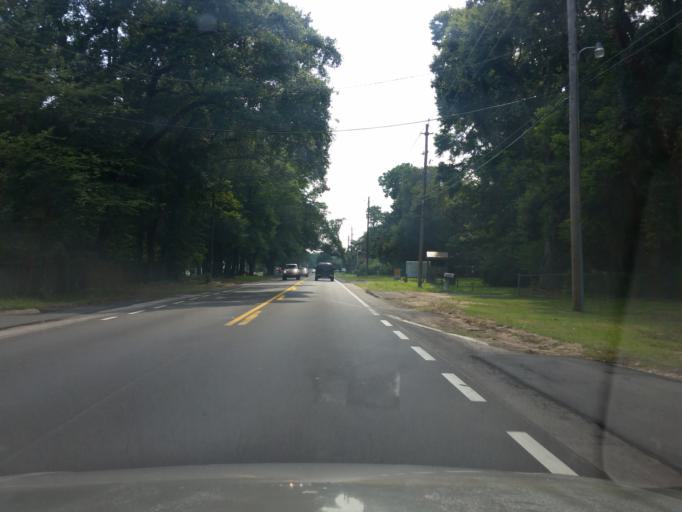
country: US
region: Florida
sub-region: Escambia County
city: Ensley
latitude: 30.5101
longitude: -87.2522
